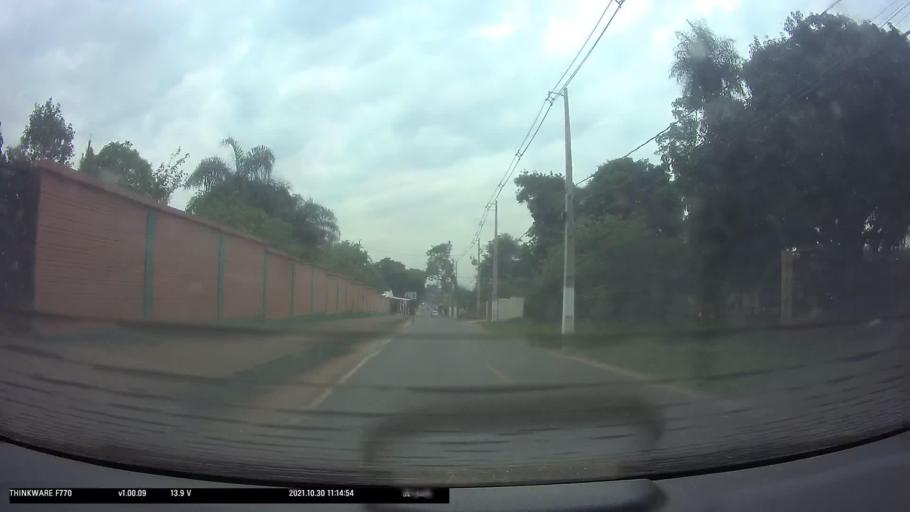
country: PY
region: Central
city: San Lorenzo
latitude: -25.3130
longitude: -57.5128
